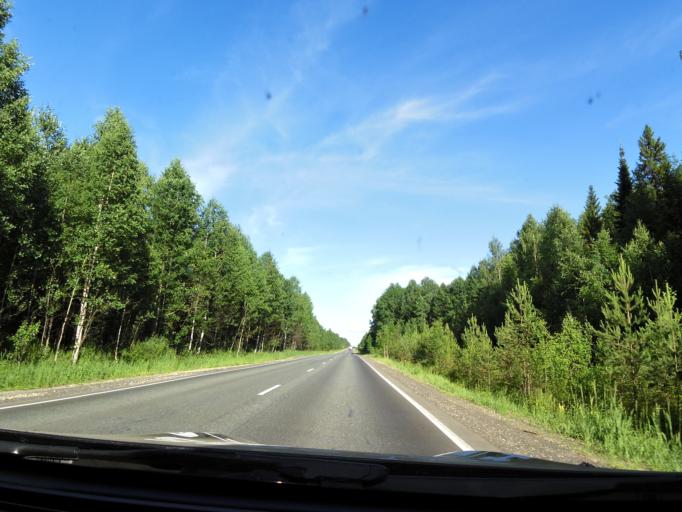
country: RU
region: Kirov
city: Chernaya Kholunitsa
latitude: 58.8716
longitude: 51.5286
